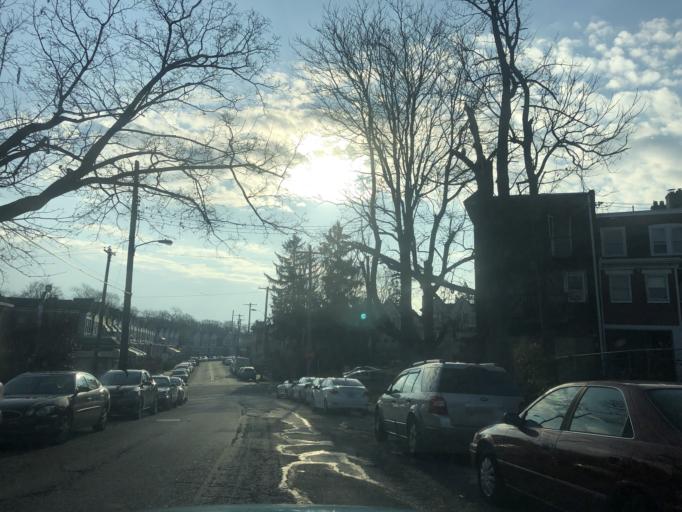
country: US
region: Pennsylvania
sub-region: Montgomery County
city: Bala-Cynwyd
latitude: 39.9889
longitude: -75.2285
